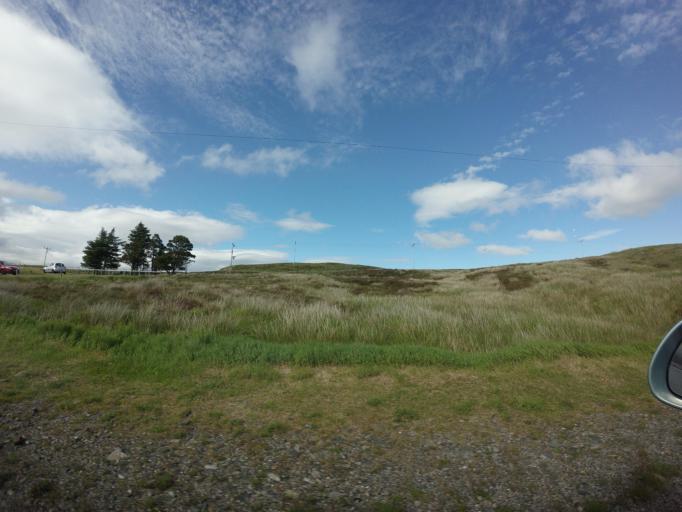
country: GB
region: Scotland
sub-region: Eilean Siar
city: Stornoway
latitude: 58.1751
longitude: -6.6119
